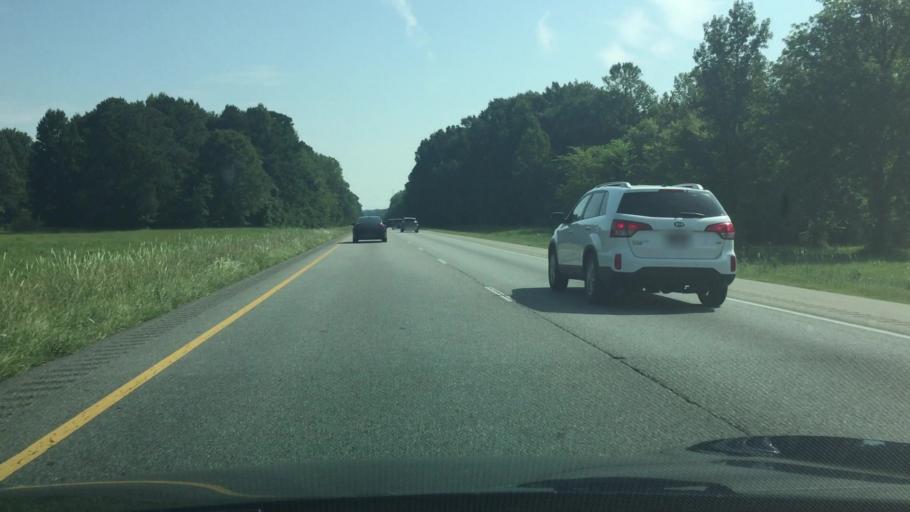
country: US
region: Alabama
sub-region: Montgomery County
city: Montgomery
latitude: 32.2170
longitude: -86.4001
